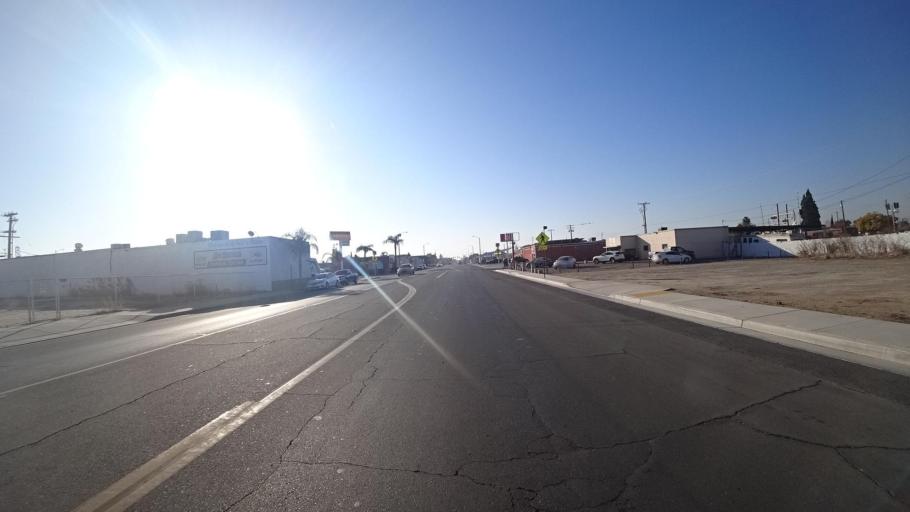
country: US
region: California
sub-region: Kern County
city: Delano
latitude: 35.7735
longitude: -119.2476
